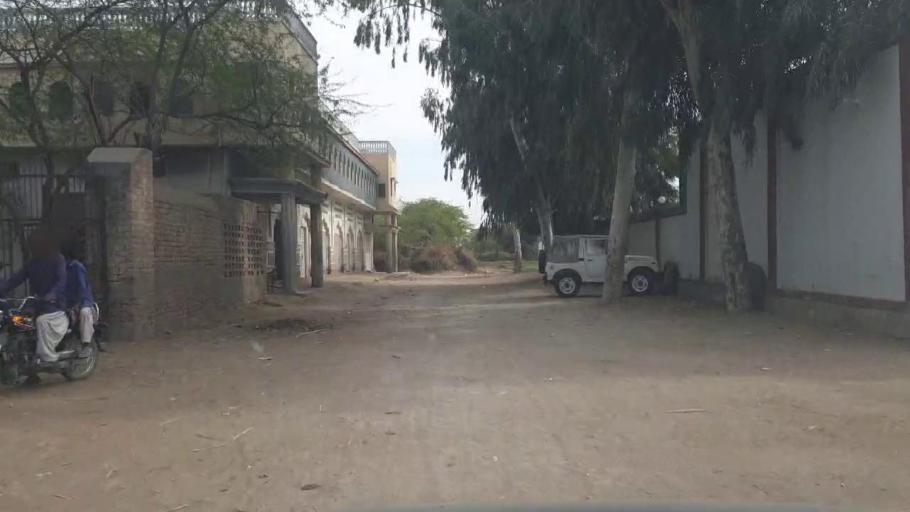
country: PK
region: Sindh
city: Kunri
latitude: 25.2836
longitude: 69.5989
